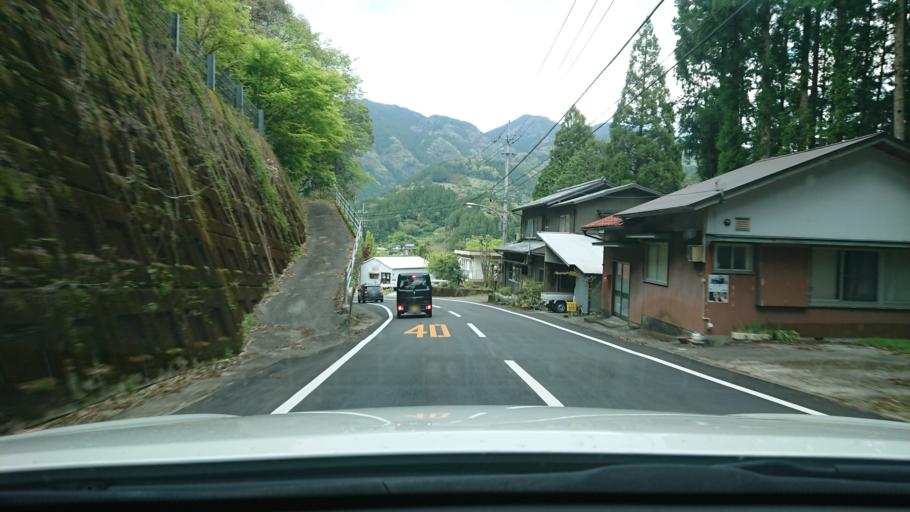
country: JP
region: Tokushima
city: Ishii
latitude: 33.9180
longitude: 134.4267
